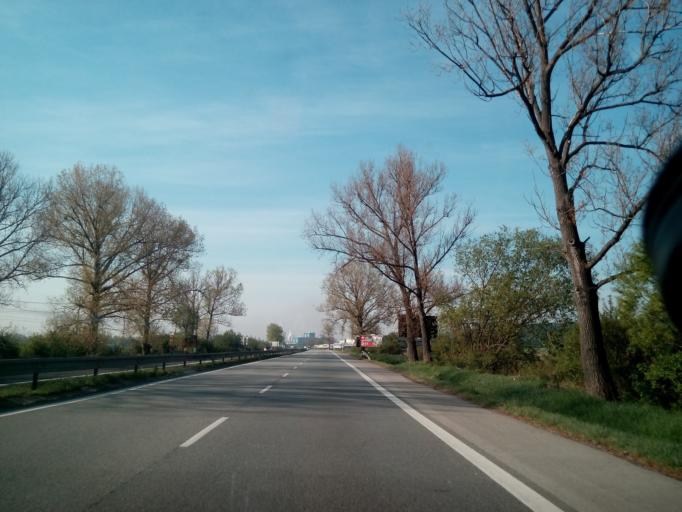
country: SK
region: Kosicky
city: Kosice
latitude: 48.6556
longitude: 21.2055
